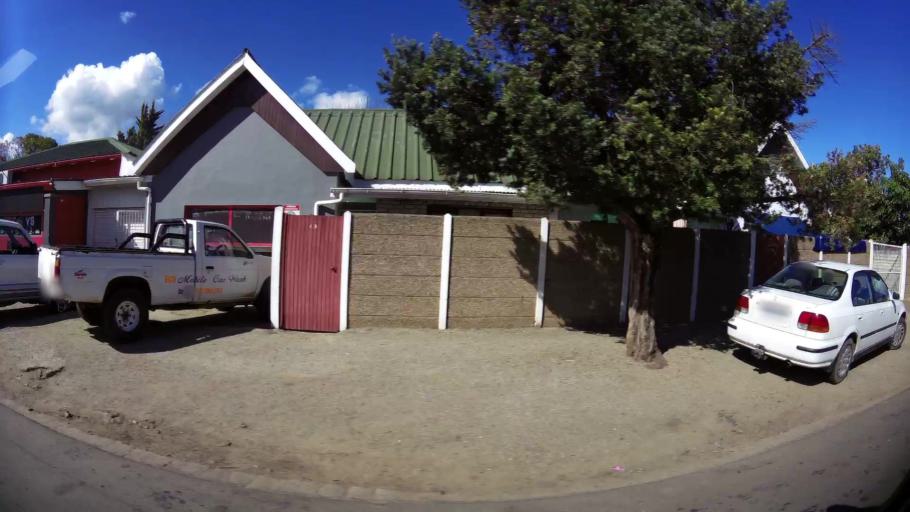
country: ZA
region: Western Cape
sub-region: Eden District Municipality
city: George
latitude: -33.9542
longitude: 22.4681
